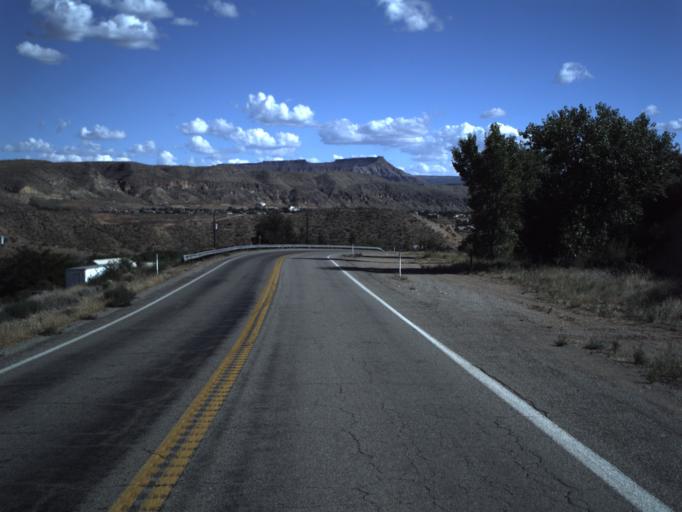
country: US
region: Utah
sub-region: Washington County
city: Toquerville
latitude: 37.2308
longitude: -113.2814
